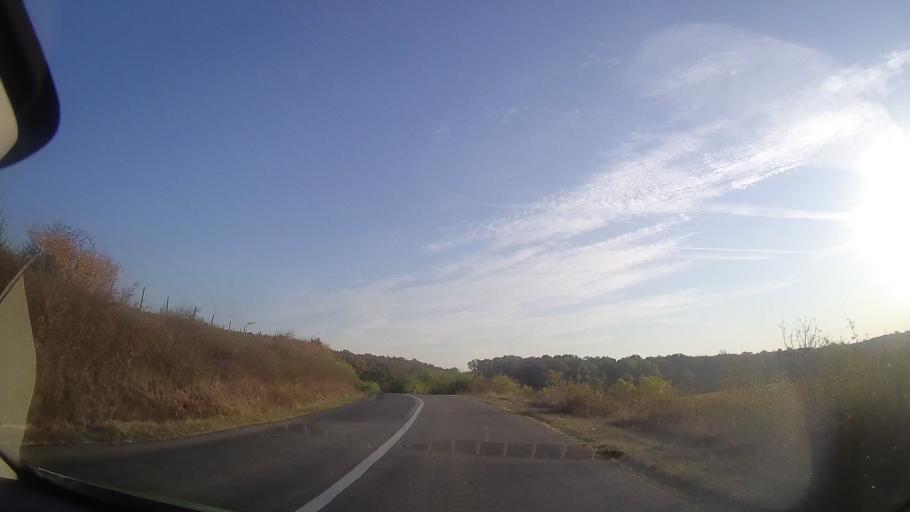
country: RO
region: Timis
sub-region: Comuna Pischia
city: Pischia
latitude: 45.9162
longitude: 21.3538
